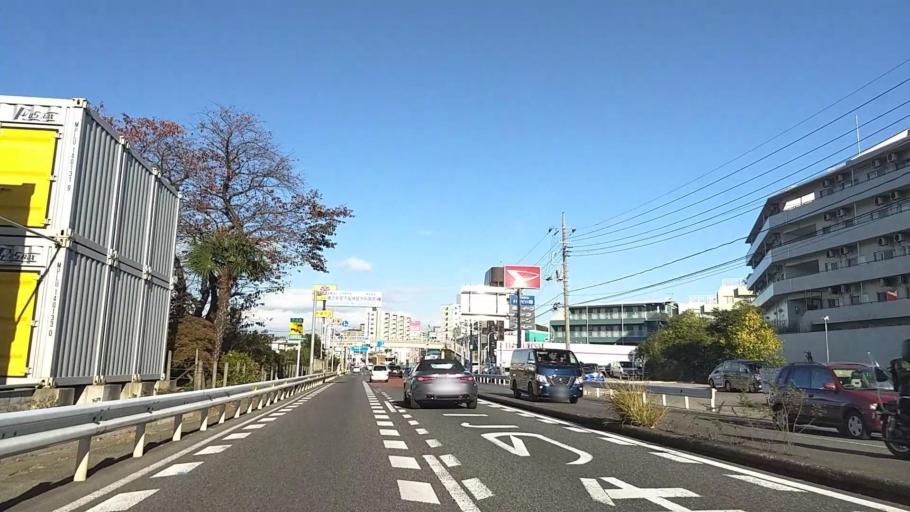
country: JP
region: Tokyo
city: Chofugaoka
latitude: 35.5601
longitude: 139.5571
